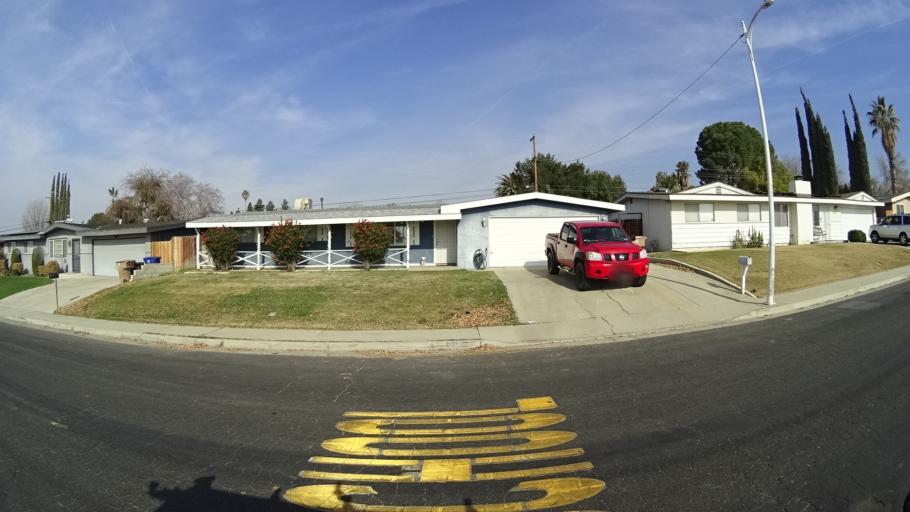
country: US
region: California
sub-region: Kern County
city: Oildale
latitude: 35.4028
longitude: -118.9570
